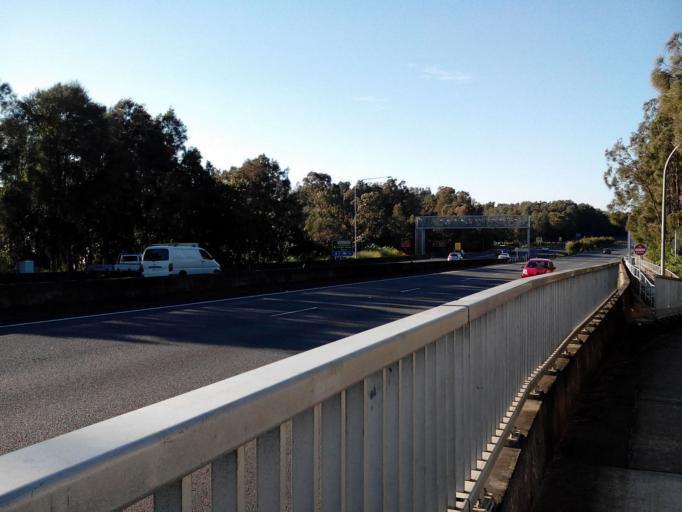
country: AU
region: New South Wales
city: Chinderah
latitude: -28.2260
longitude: 153.5565
